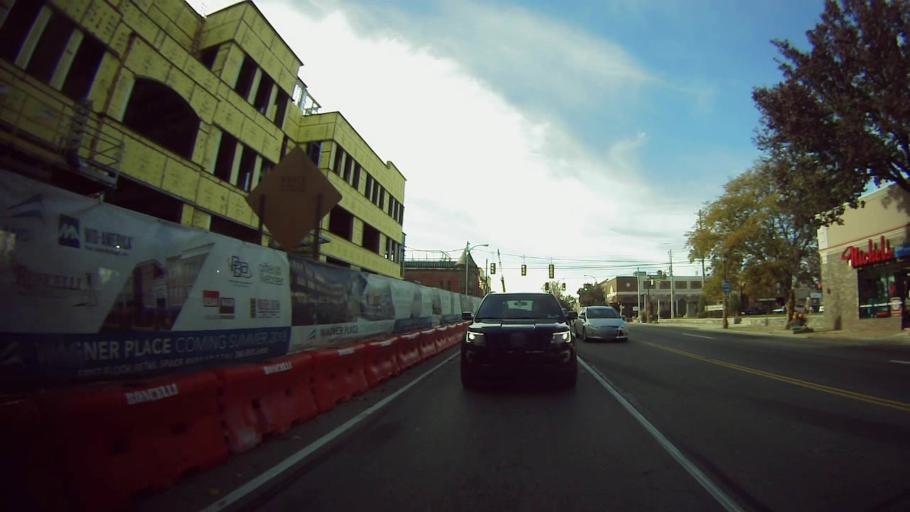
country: US
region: Michigan
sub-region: Wayne County
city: Dearborn Heights
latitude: 42.3063
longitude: -83.2433
